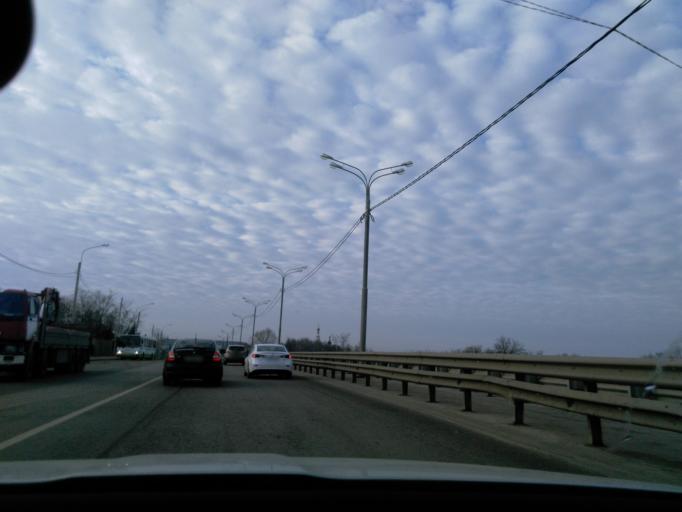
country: RU
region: Moskovskaya
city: Dolgoprudnyy
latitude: 55.9238
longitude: 37.4930
